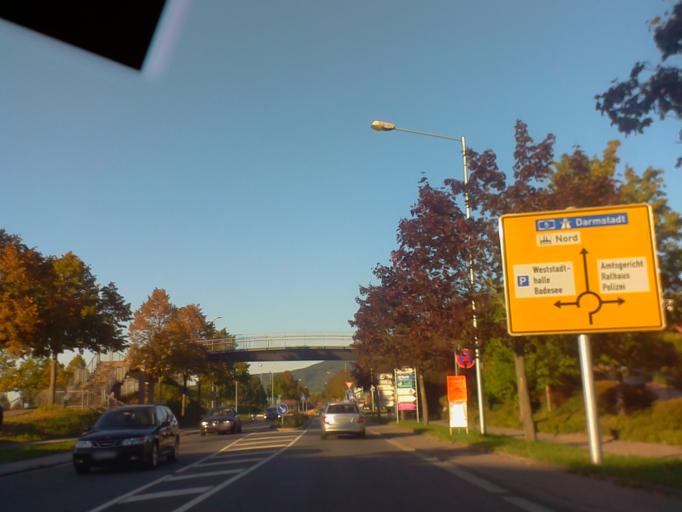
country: DE
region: Hesse
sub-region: Regierungsbezirk Darmstadt
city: Bensheim
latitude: 49.6867
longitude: 8.6064
